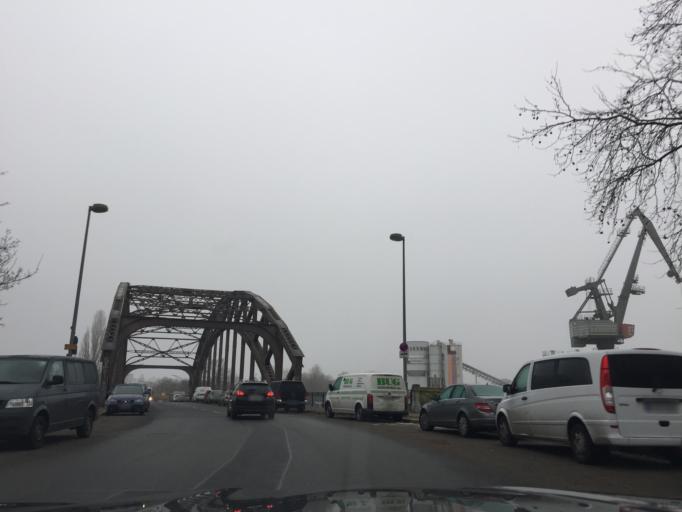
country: DE
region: Berlin
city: Wilhelmstadt
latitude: 52.5239
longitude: 13.2036
